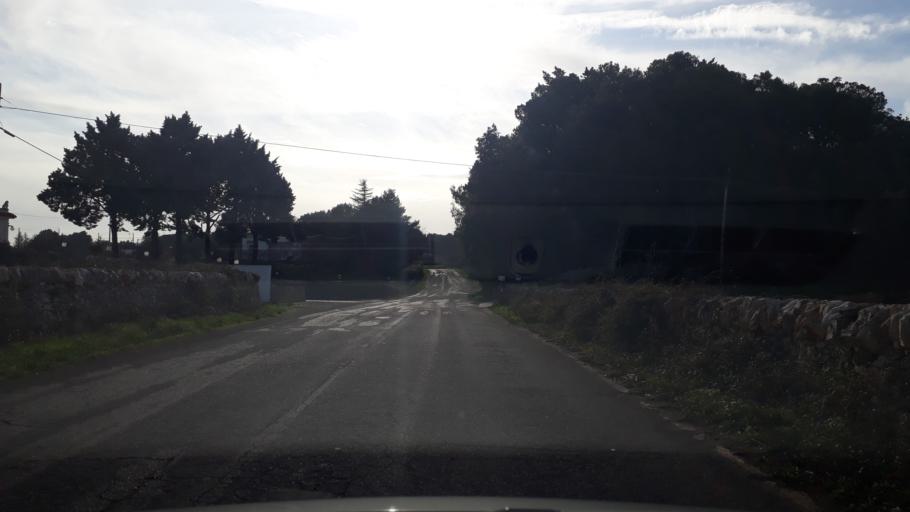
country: IT
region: Apulia
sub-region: Provincia di Taranto
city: Martina Franca
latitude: 40.6747
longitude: 17.3624
